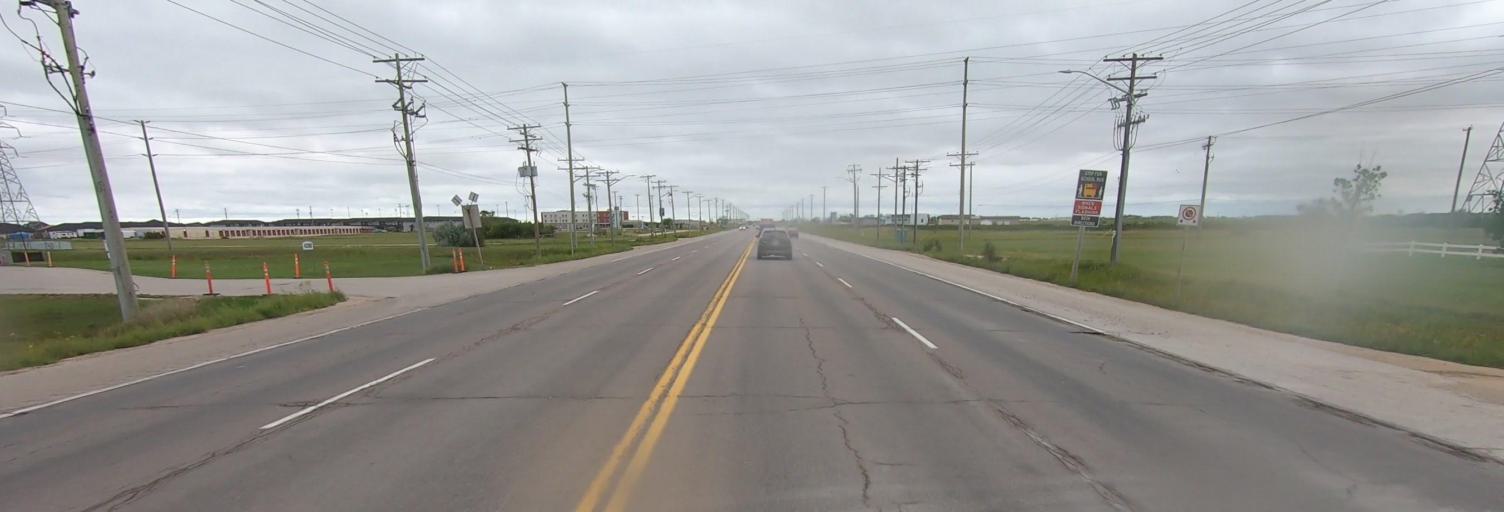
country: CA
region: Manitoba
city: Headingley
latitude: 49.8781
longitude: -97.3463
